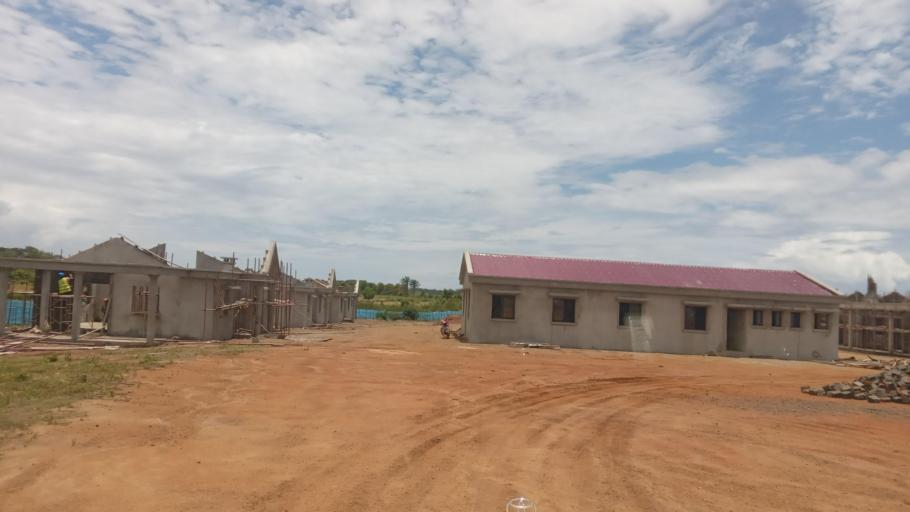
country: MG
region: Atsimo-Atsinanana
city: Vohipaho
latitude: -23.7907
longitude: 47.5521
